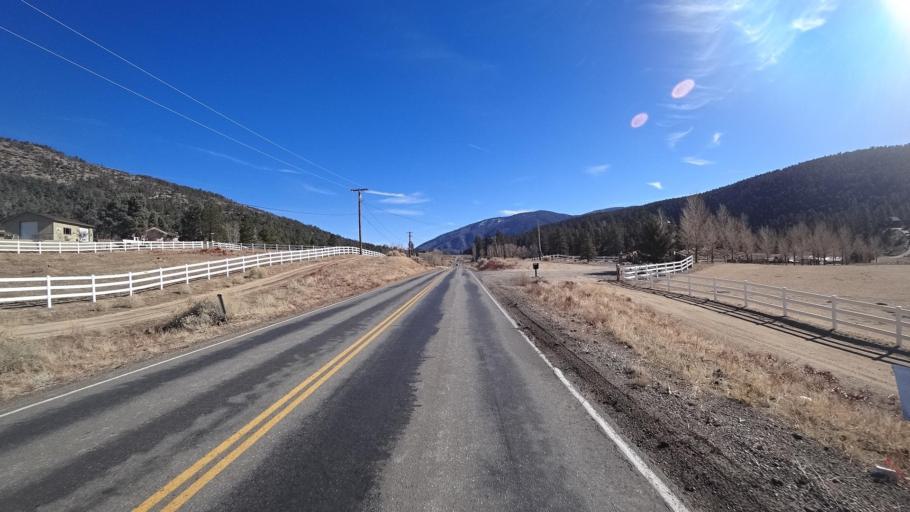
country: US
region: California
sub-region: Kern County
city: Frazier Park
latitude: 34.8303
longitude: -119.0267
